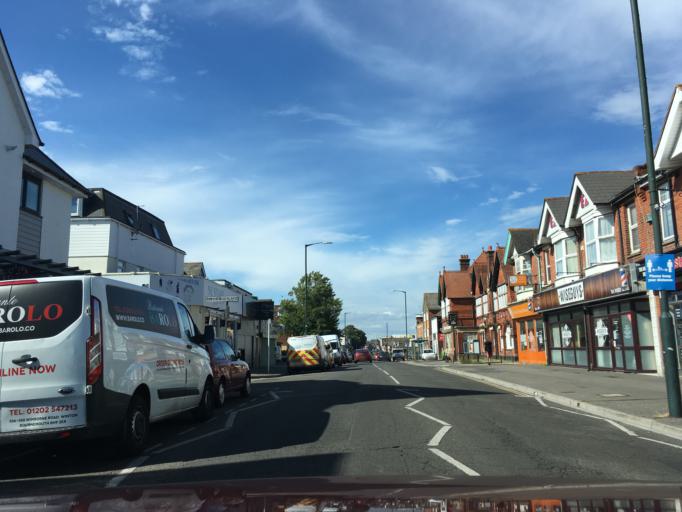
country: GB
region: England
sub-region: Bournemouth
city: Bournemouth
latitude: 50.7457
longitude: -1.8782
